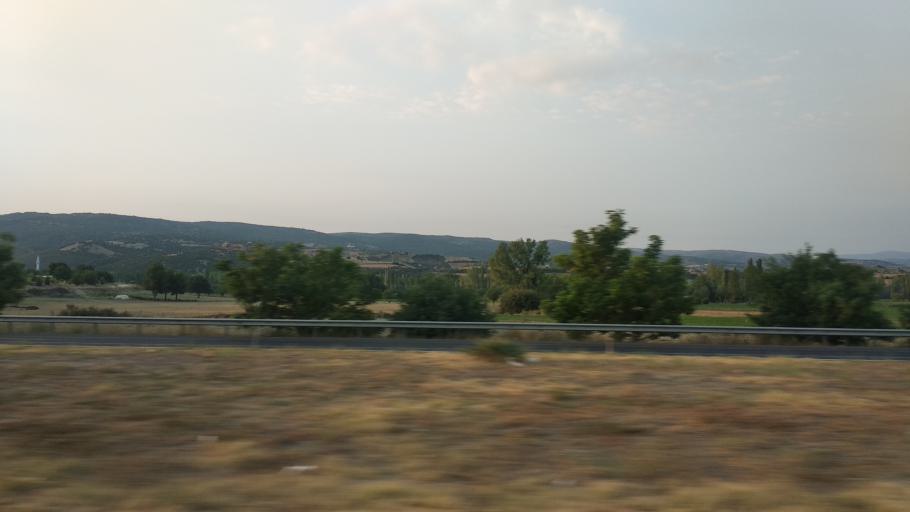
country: TR
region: Manisa
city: Selendi
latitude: 38.6215
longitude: 28.9195
